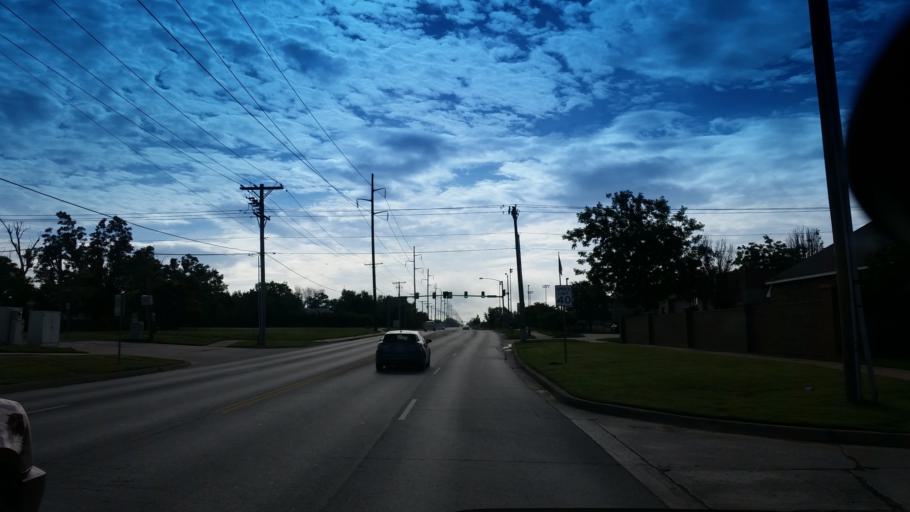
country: US
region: Oklahoma
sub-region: Oklahoma County
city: Edmond
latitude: 35.6675
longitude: -97.5057
